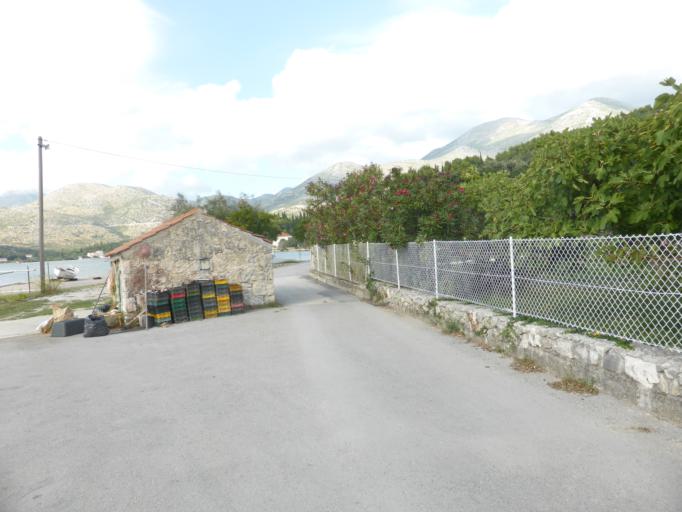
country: HR
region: Dubrovacko-Neretvanska
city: Podgora
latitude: 42.7740
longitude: 17.8838
